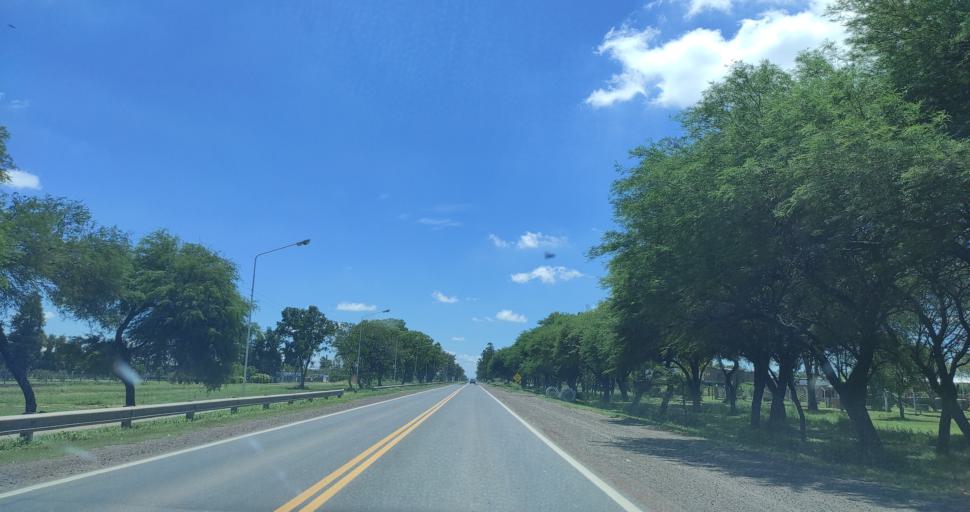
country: AR
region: Chaco
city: Las Brenas
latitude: -27.1028
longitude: -61.0694
